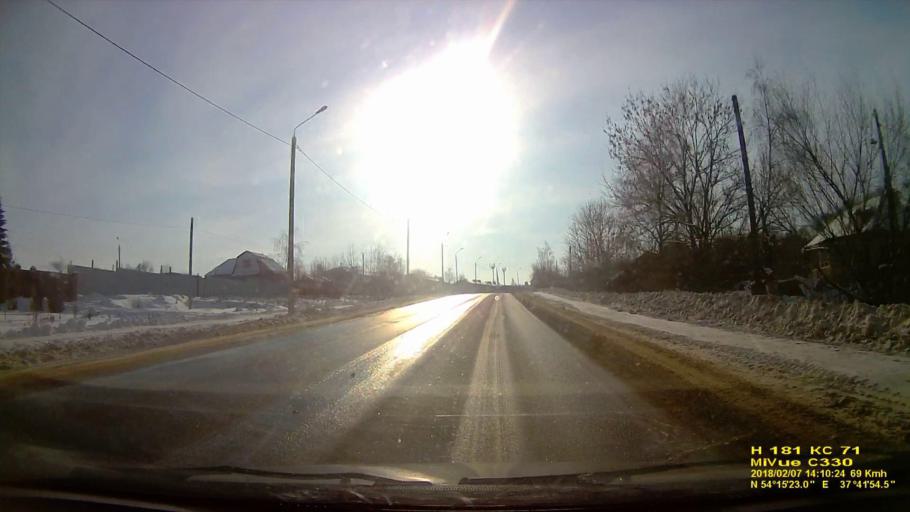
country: RU
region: Tula
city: Gorelki
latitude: 54.2563
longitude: 37.6983
